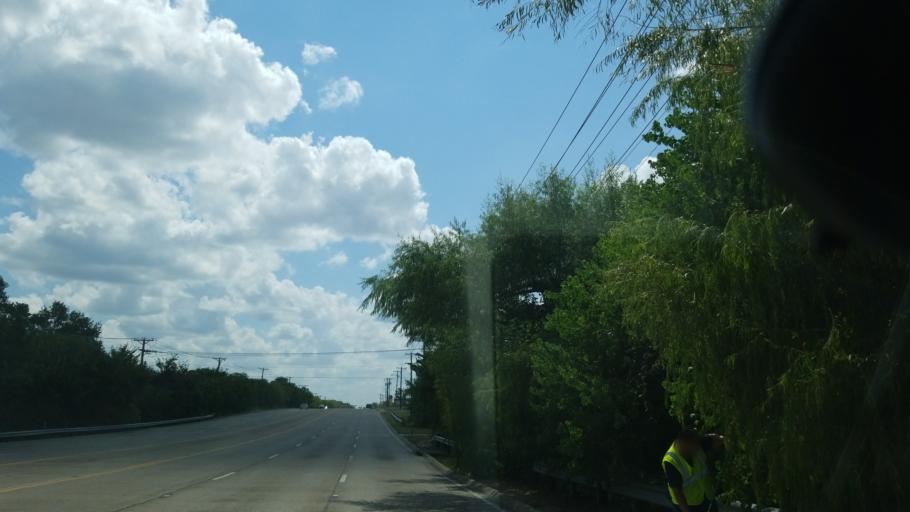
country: US
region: Texas
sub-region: Dallas County
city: Grand Prairie
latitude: 32.7255
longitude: -96.9942
